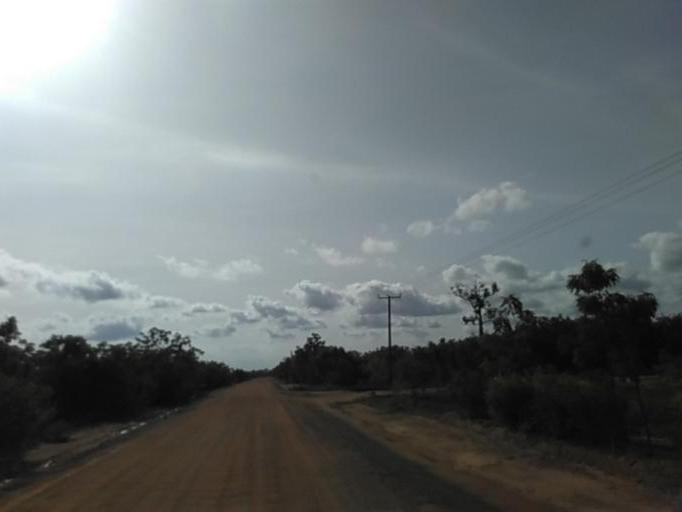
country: GH
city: Akropong
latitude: 6.0880
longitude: 0.2662
